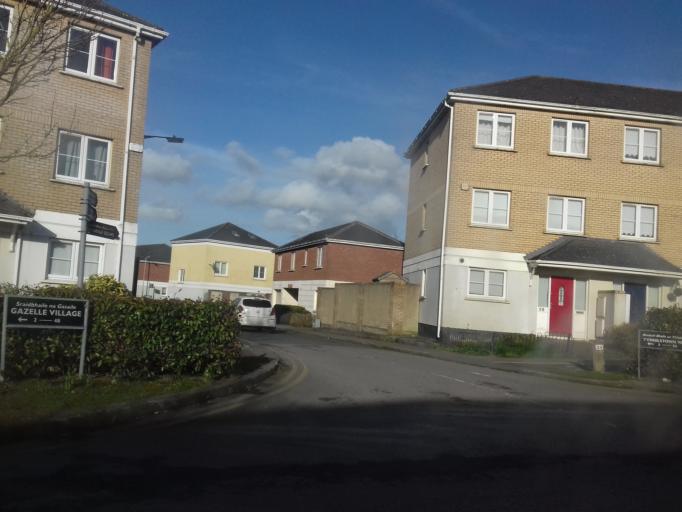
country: IE
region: Leinster
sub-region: Fingal County
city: Blanchardstown
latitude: 53.4180
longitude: -6.3864
